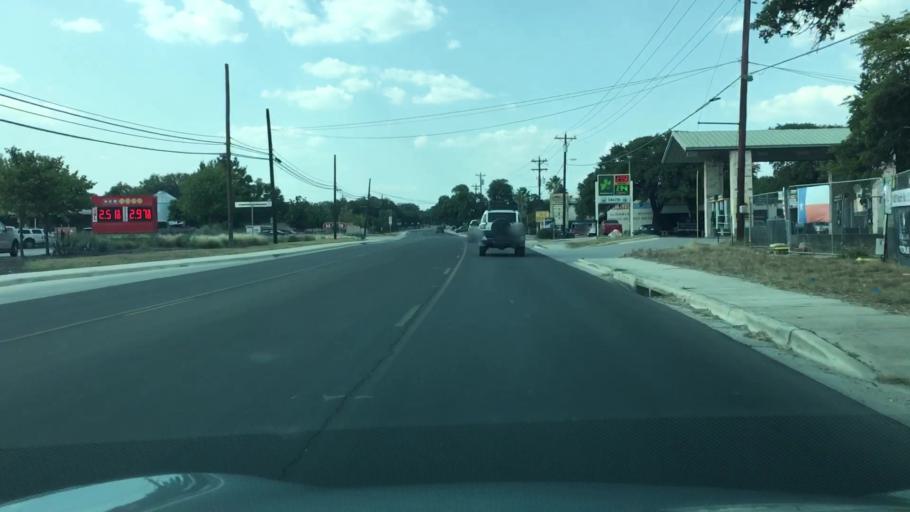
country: US
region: Texas
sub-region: Hays County
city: Wimberley
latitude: 30.0013
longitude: -98.1017
